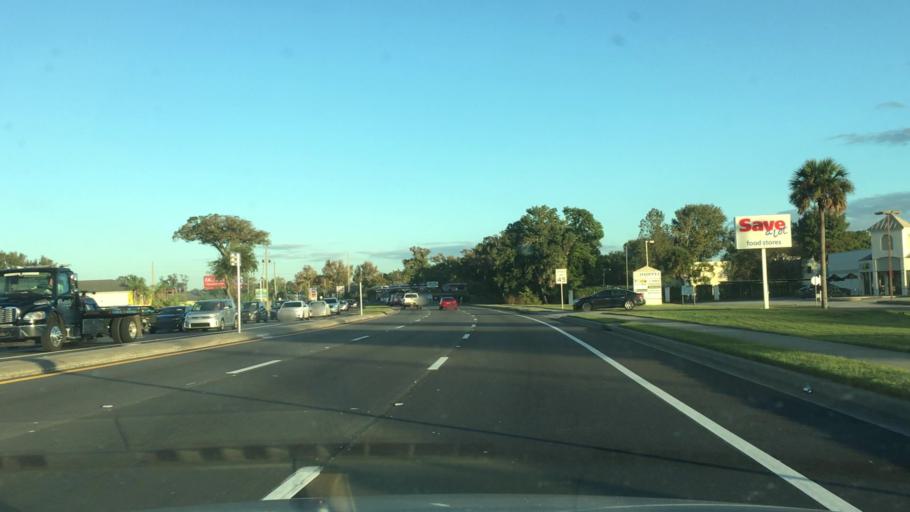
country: US
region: Florida
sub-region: Volusia County
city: Holly Hill
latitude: 29.2394
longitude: -81.0579
